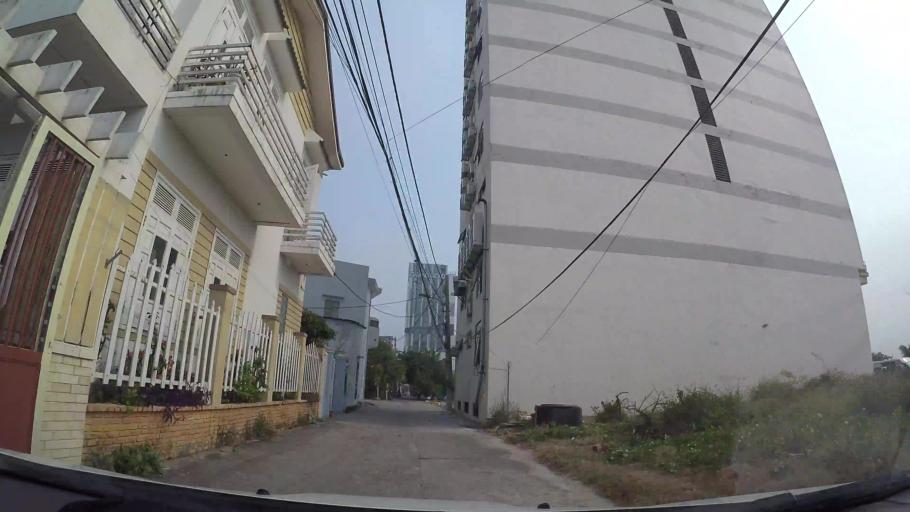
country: VN
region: Da Nang
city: Son Tra
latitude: 16.0920
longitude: 108.2506
